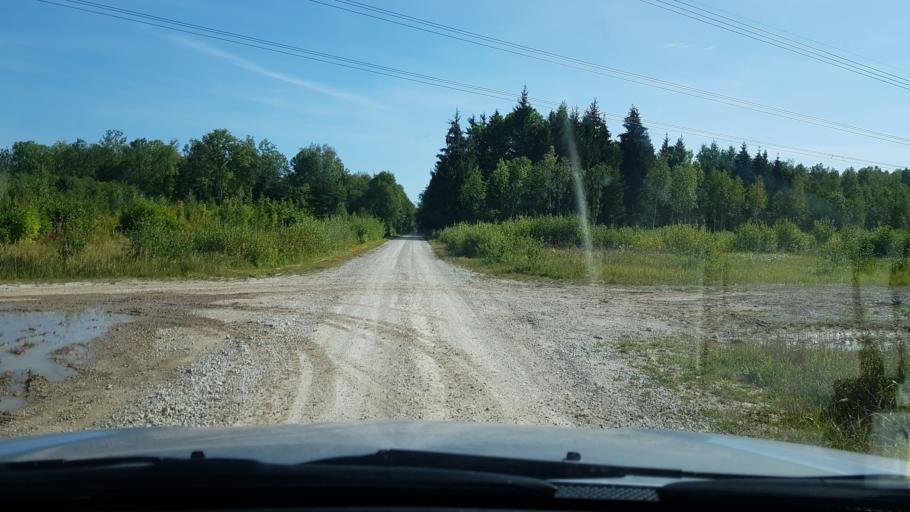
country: EE
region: Ida-Virumaa
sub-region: Sillamaee linn
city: Sillamae
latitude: 59.3324
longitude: 27.7621
